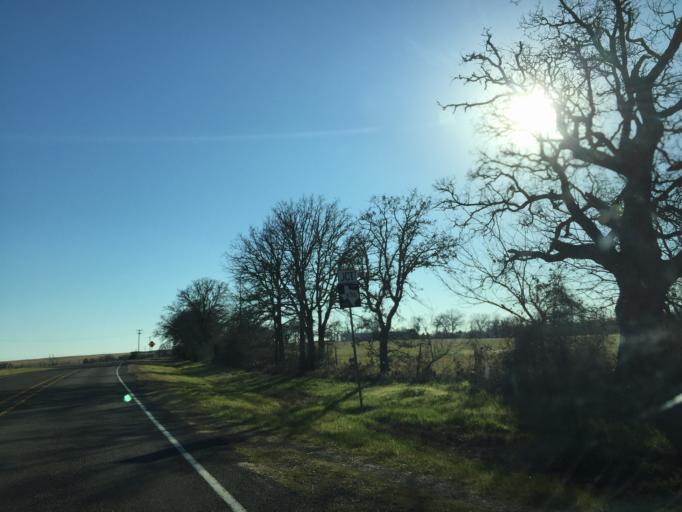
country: US
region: Texas
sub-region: Bastrop County
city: Elgin
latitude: 30.3841
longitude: -97.2438
